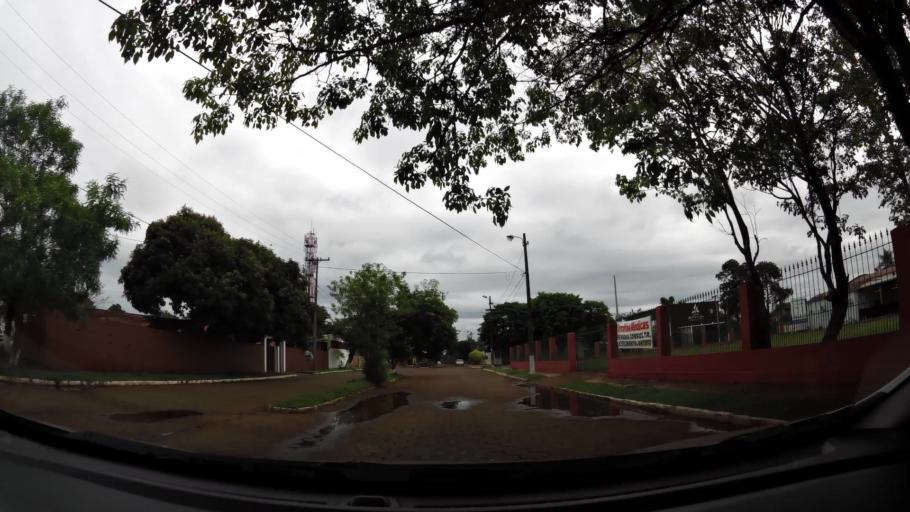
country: PY
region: Alto Parana
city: Ciudad del Este
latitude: -25.4016
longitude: -54.6420
